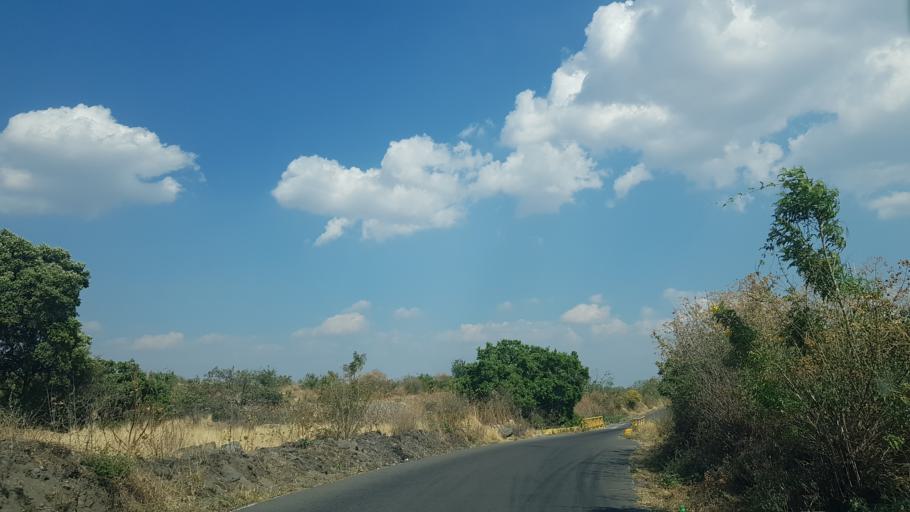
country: MX
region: Puebla
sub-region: Atlixco
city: Colonia Agricola de Ocotepec (Colonia San Jose)
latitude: 18.9211
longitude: -98.5338
